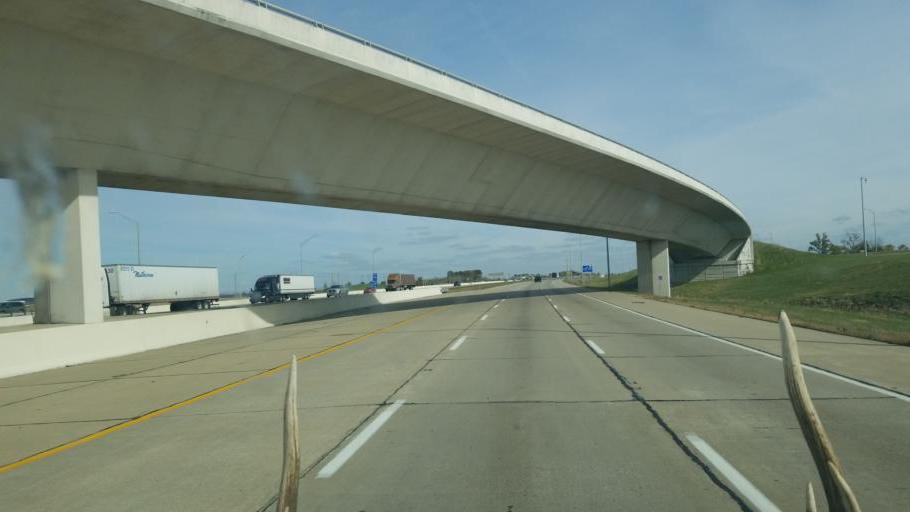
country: US
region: Indiana
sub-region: Hendricks County
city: Plainfield
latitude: 39.6912
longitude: -86.3153
